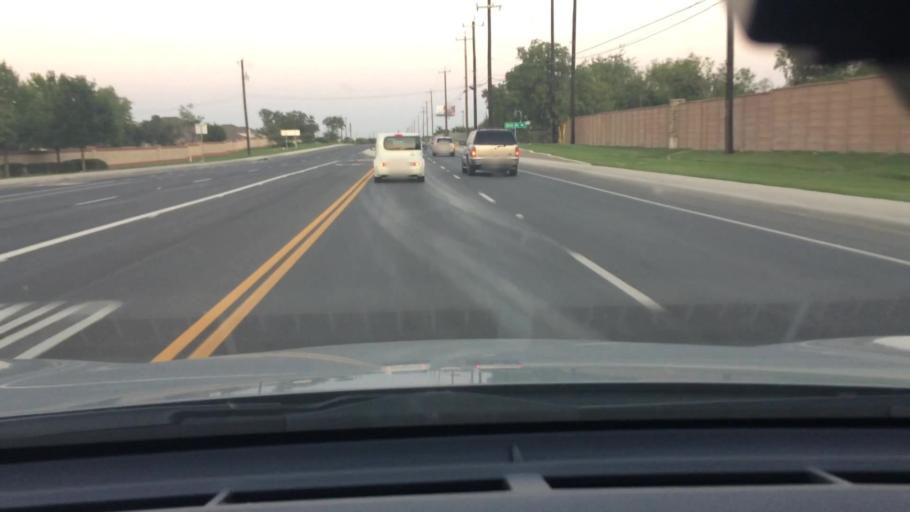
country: US
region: Texas
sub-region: Bexar County
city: Helotes
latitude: 29.5128
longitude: -98.7530
